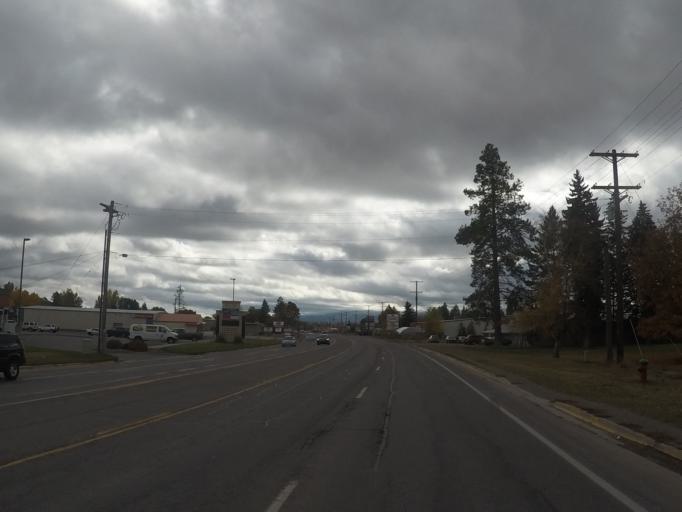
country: US
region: Montana
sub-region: Flathead County
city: Evergreen
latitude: 48.2240
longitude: -114.2771
